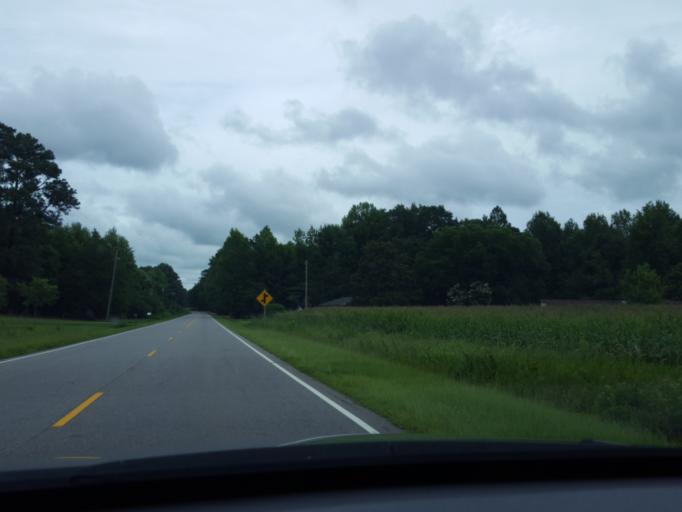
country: US
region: North Carolina
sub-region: Martin County
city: Williamston
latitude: 35.7189
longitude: -76.9835
